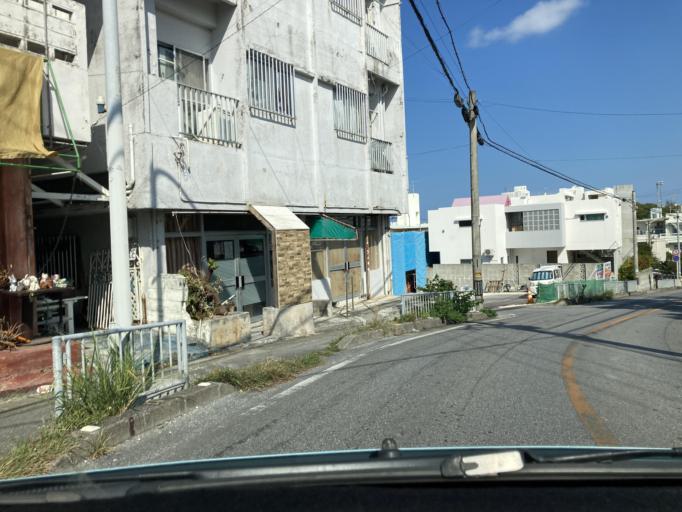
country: JP
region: Okinawa
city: Tomigusuku
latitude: 26.1855
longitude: 127.6664
